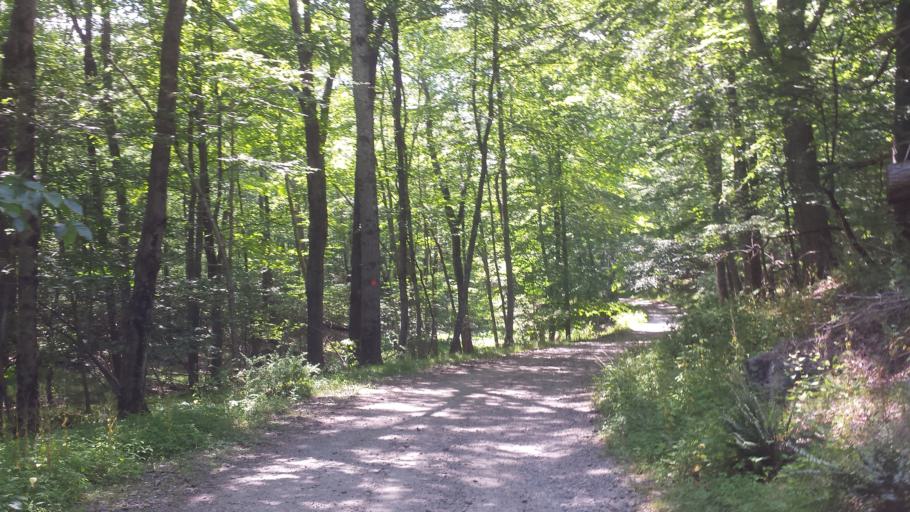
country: US
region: Connecticut
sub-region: Fairfield County
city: Ridgefield
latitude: 41.3091
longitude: -73.5531
